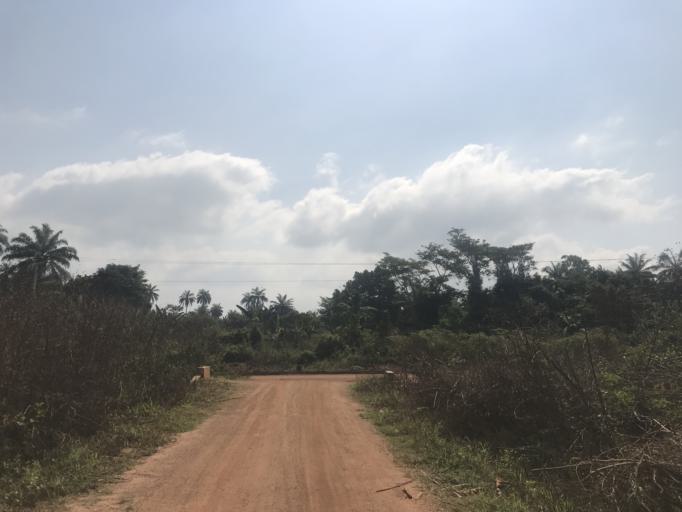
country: NG
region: Osun
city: Ikirun
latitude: 7.8477
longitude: 4.6325
